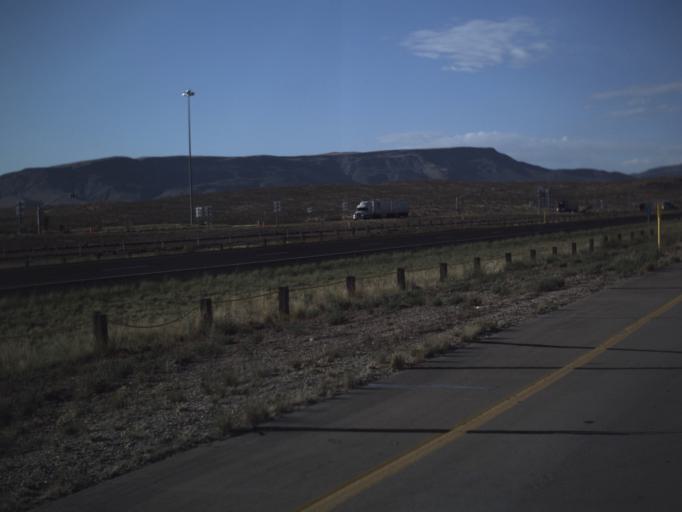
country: US
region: Utah
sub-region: Washington County
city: Saint George
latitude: 37.0139
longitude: -113.6146
